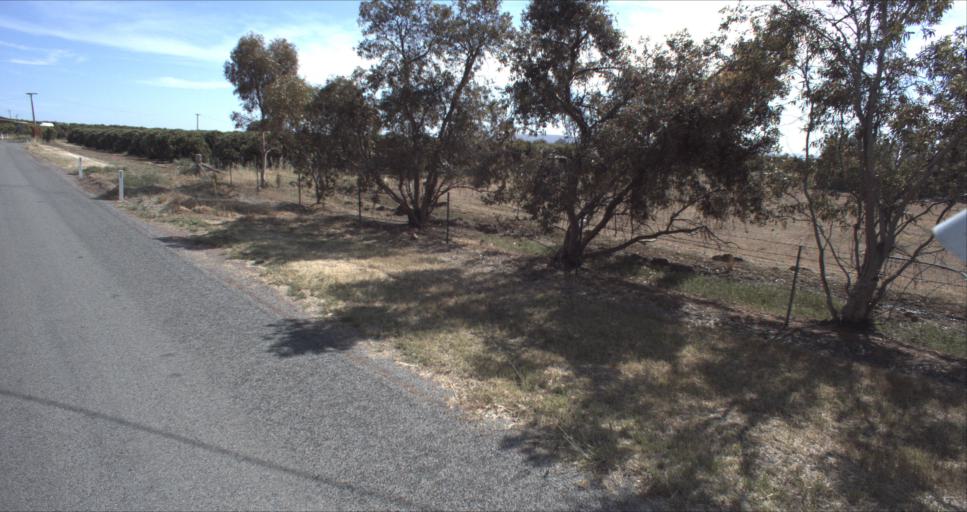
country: AU
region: New South Wales
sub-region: Leeton
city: Leeton
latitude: -34.5713
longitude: 146.4658
